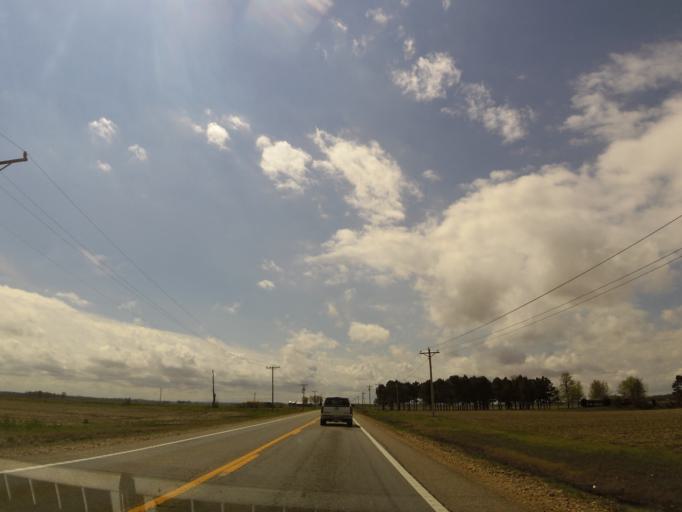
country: US
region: Arkansas
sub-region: Clay County
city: Corning
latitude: 36.3692
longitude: -90.5247
